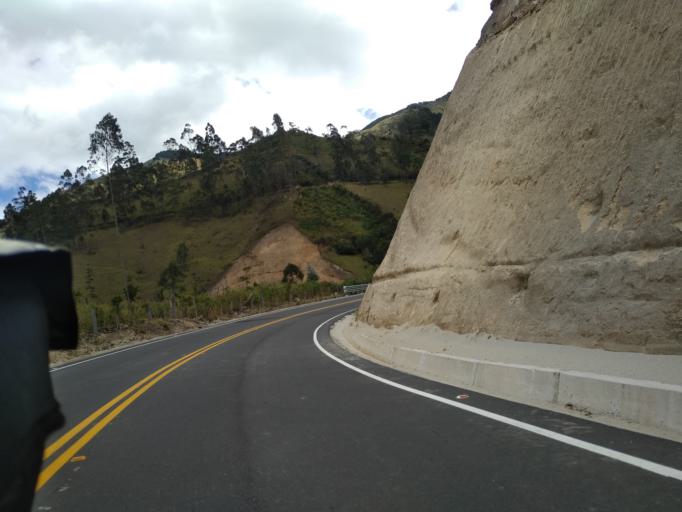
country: EC
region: Cotopaxi
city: Saquisili
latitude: -0.7270
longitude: -78.8977
